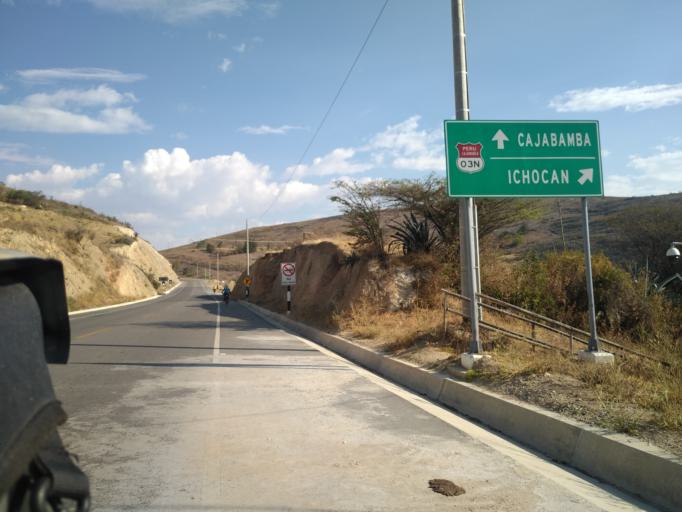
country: PE
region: Cajamarca
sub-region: San Marcos
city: San Marcos
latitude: -7.3737
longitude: -78.1288
